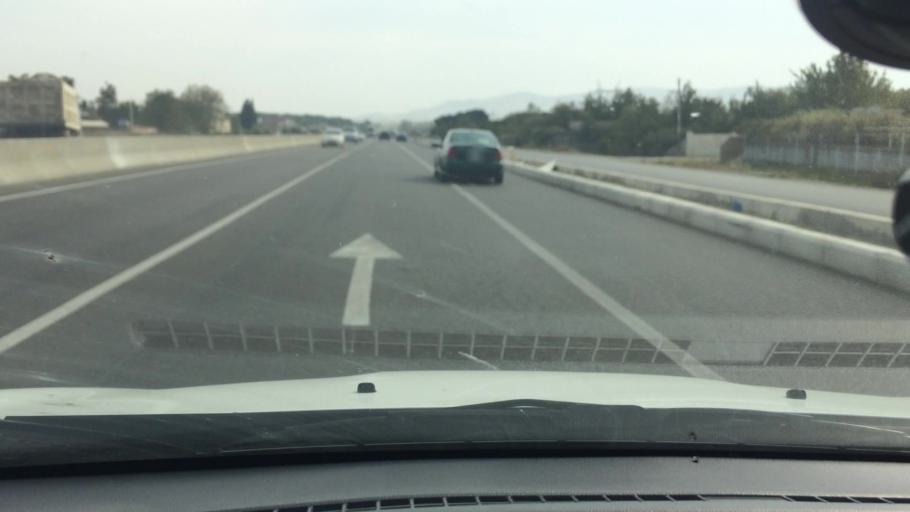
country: GE
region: T'bilisi
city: Tbilisi
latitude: 41.6368
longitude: 44.9161
